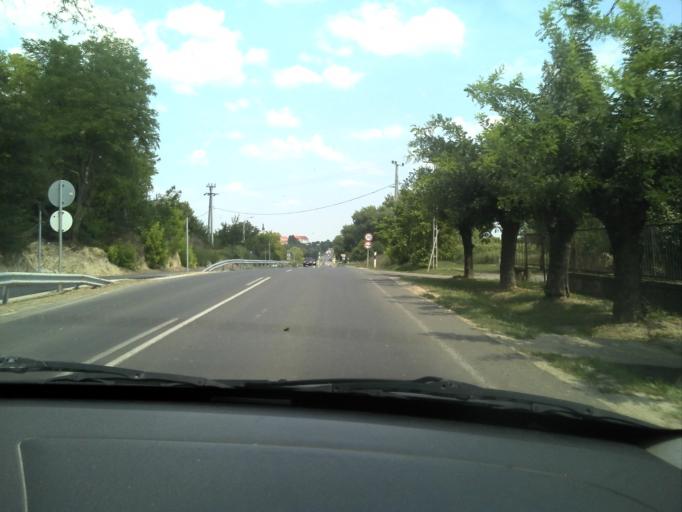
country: HU
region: Tolna
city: Tamasi
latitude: 46.6248
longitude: 18.2695
